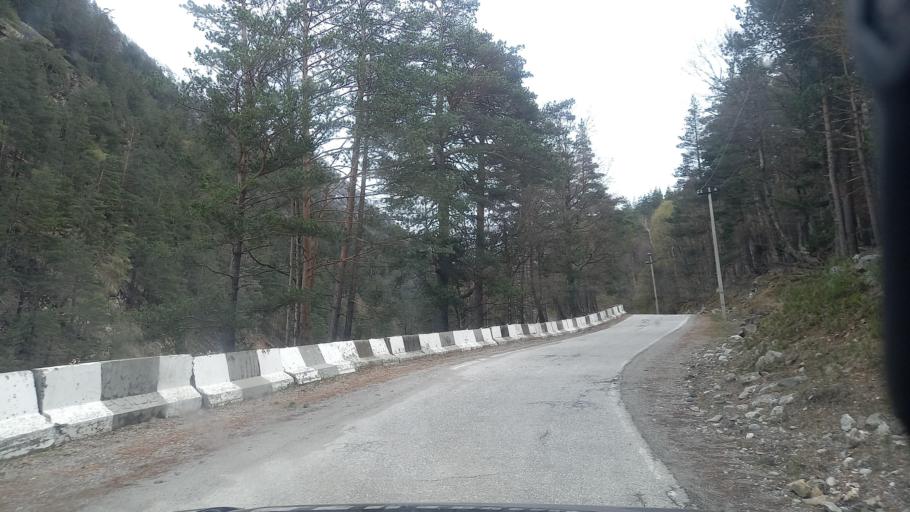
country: RU
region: Kabardino-Balkariya
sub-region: El'brusskiy Rayon
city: El'brus
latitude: 43.2420
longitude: 42.6394
